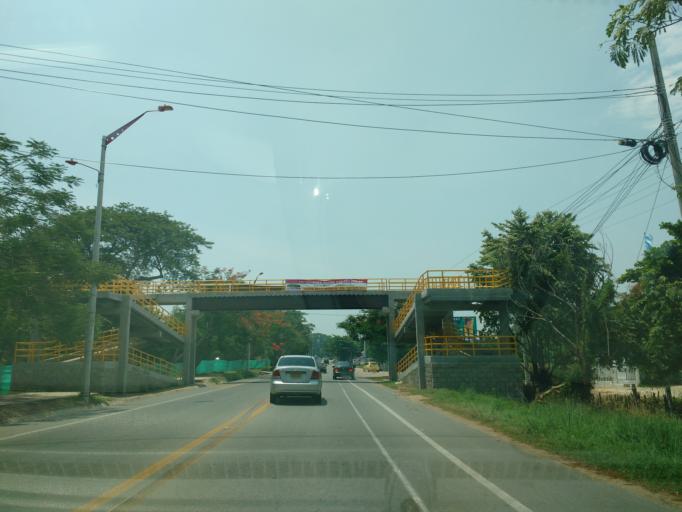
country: CO
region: Cundinamarca
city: Ricaurte
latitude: 4.2787
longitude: -74.7639
